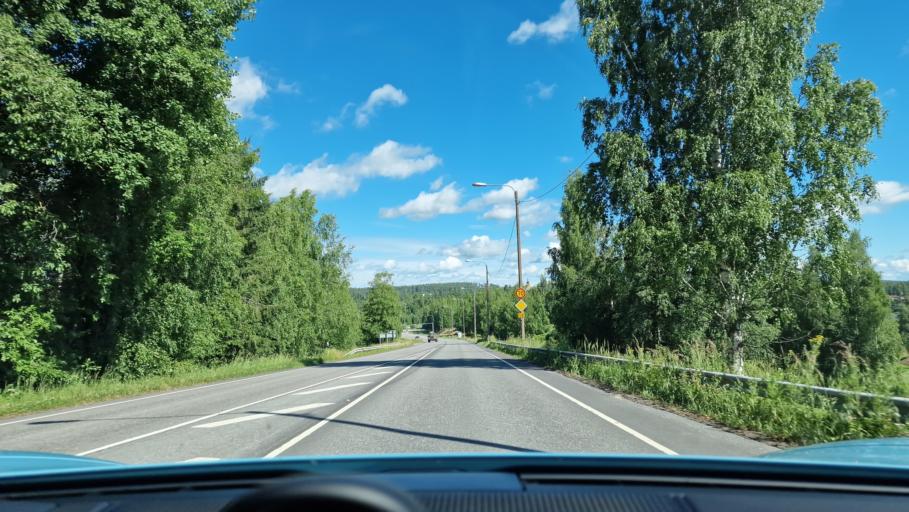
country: FI
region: Pirkanmaa
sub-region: Tampere
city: Orivesi
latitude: 61.6651
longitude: 24.3572
